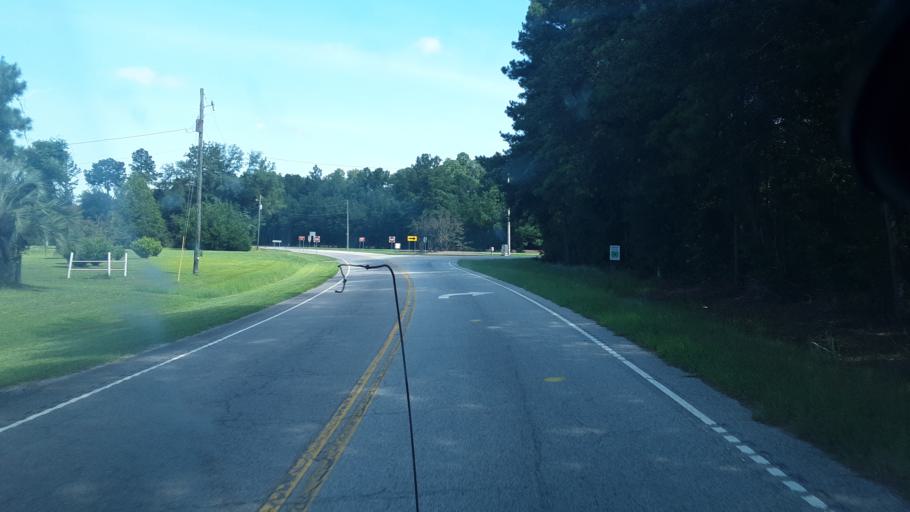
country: US
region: South Carolina
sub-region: Hampton County
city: Varnville
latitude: 32.8288
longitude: -81.0515
